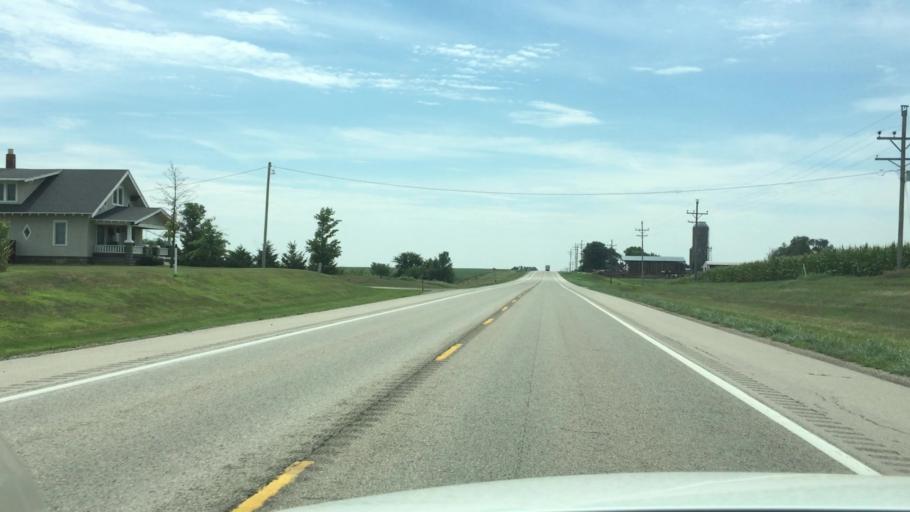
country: US
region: Kansas
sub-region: Nemaha County
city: Sabetha
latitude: 39.7772
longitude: -95.7295
